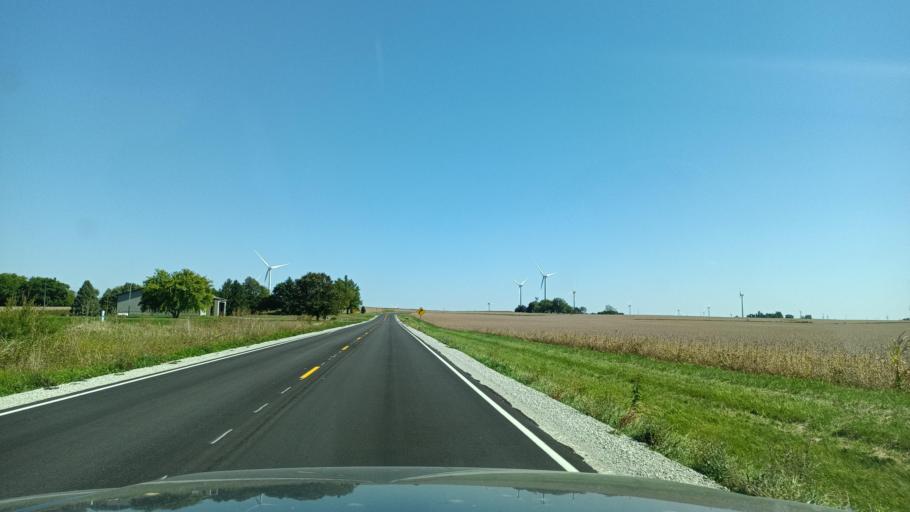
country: US
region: Illinois
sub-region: McLean County
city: Danvers
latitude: 40.5828
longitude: -89.1091
